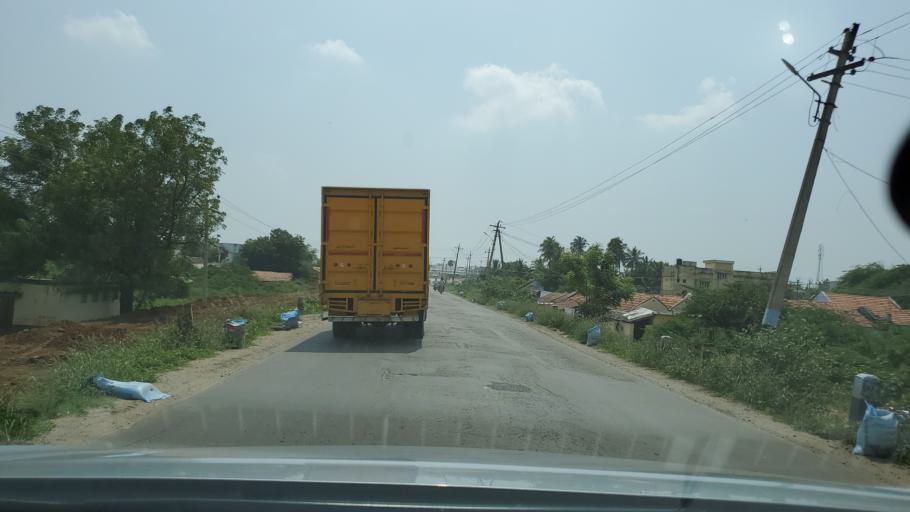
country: IN
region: Tamil Nadu
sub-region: Tiruppur
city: Dharapuram
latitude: 10.7455
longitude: 77.5189
